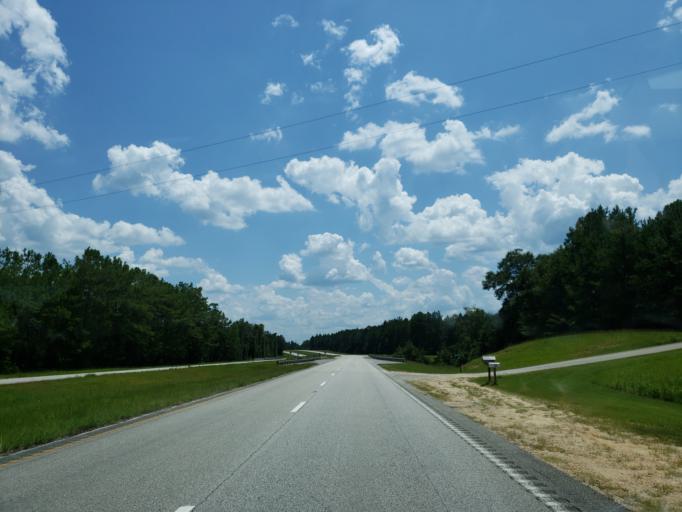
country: US
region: Mississippi
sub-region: Greene County
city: Leakesville
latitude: 31.3288
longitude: -88.5044
